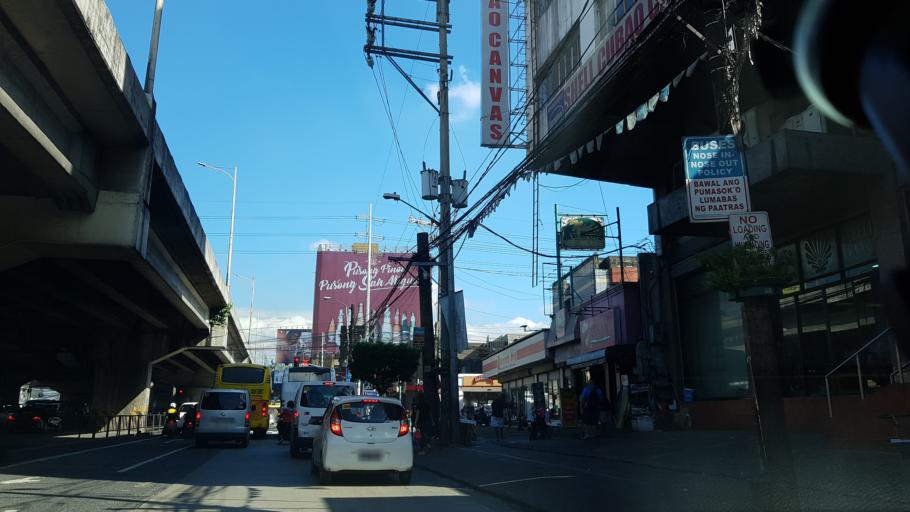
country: PH
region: Metro Manila
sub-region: Quezon City
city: Quezon City
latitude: 14.6302
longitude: 121.0463
